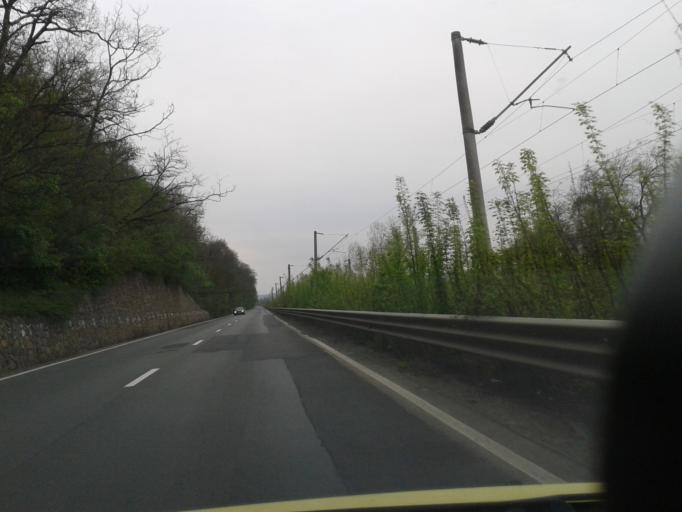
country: RO
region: Arad
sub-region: Comuna Conop
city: Conop
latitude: 46.0992
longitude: 21.8849
